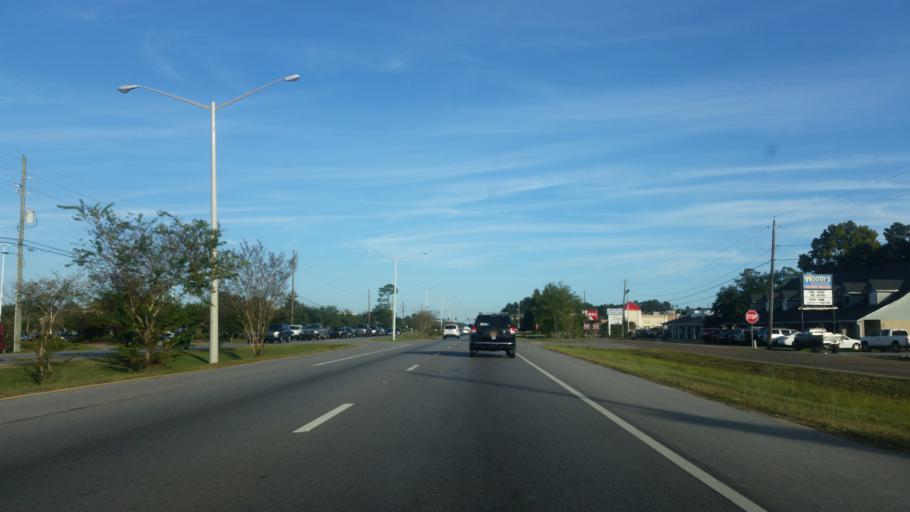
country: US
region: Mississippi
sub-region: Jackson County
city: Gulf Park Estates
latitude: 30.4133
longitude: -88.7869
